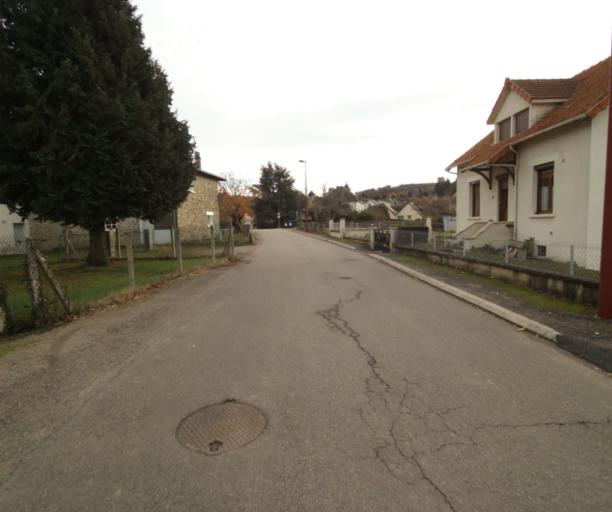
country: FR
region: Limousin
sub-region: Departement de la Correze
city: Sainte-Fortunade
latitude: 45.2107
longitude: 1.7713
